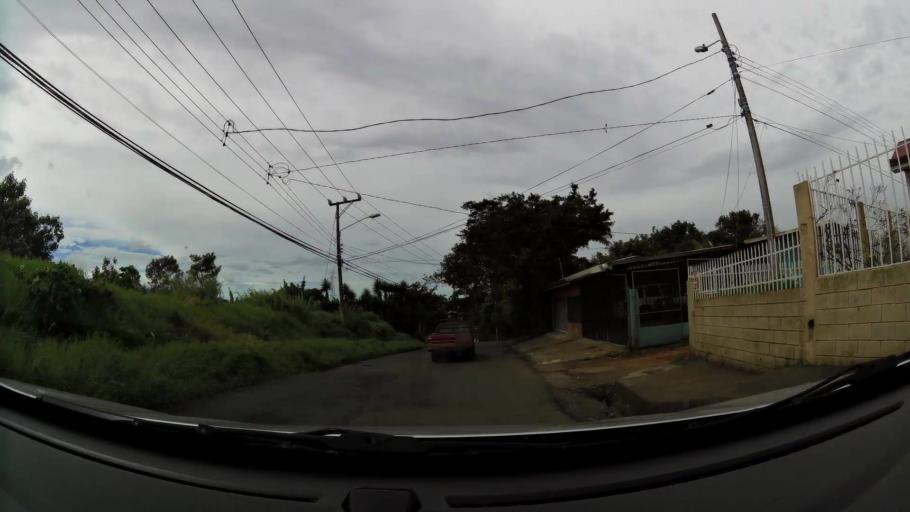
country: CR
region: San Jose
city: Ipis
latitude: 9.9593
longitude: -84.0169
